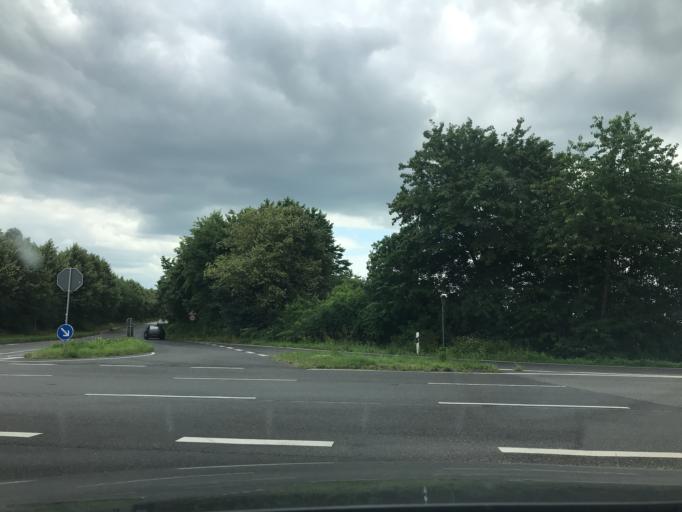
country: DE
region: North Rhine-Westphalia
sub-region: Regierungsbezirk Dusseldorf
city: Neubrueck
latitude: 51.1678
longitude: 6.6552
